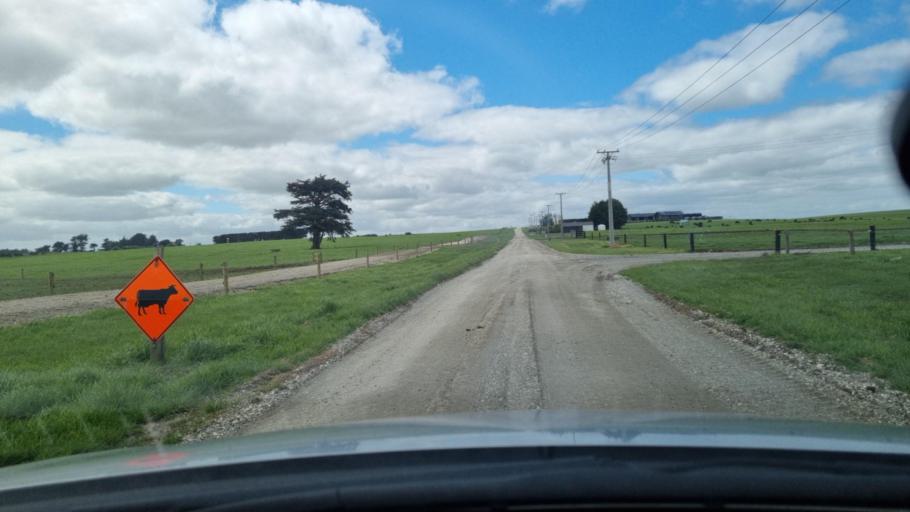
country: NZ
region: Southland
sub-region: Invercargill City
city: Invercargill
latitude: -46.4506
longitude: 168.4104
